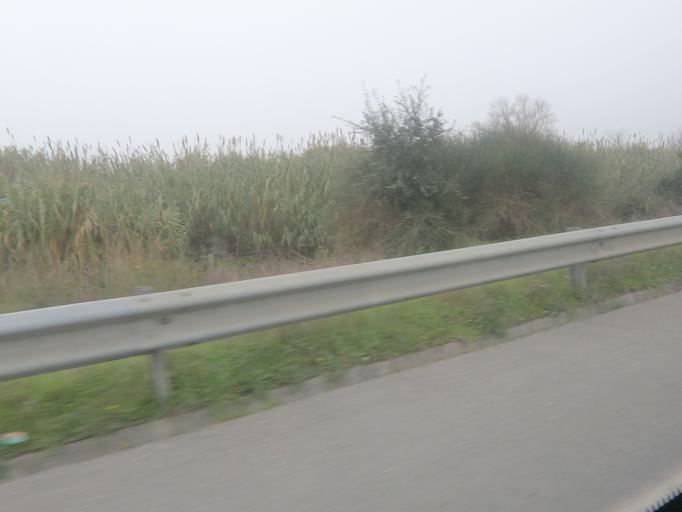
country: PT
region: Setubal
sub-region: Montijo
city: Montijo
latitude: 38.6833
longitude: -8.9485
